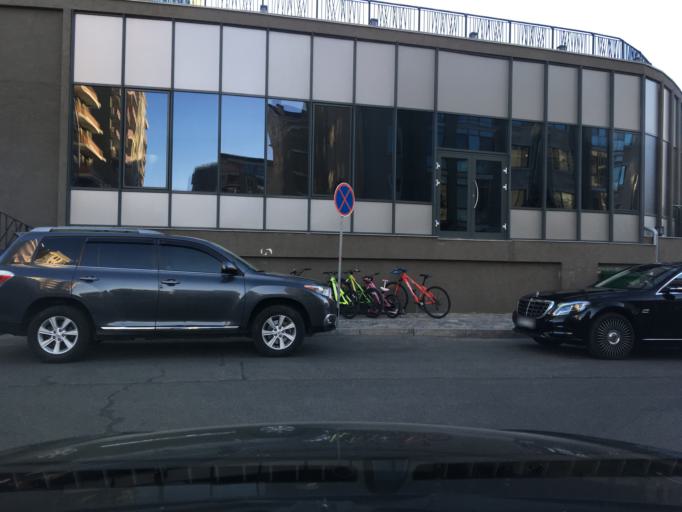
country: MN
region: Ulaanbaatar
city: Ulaanbaatar
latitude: 47.8898
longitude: 106.9321
